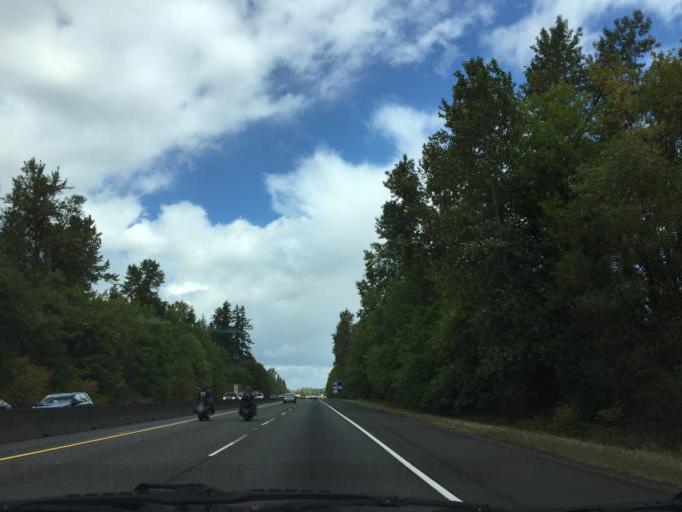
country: US
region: Washington
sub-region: Cowlitz County
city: Castle Rock
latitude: 46.3780
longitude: -122.9051
